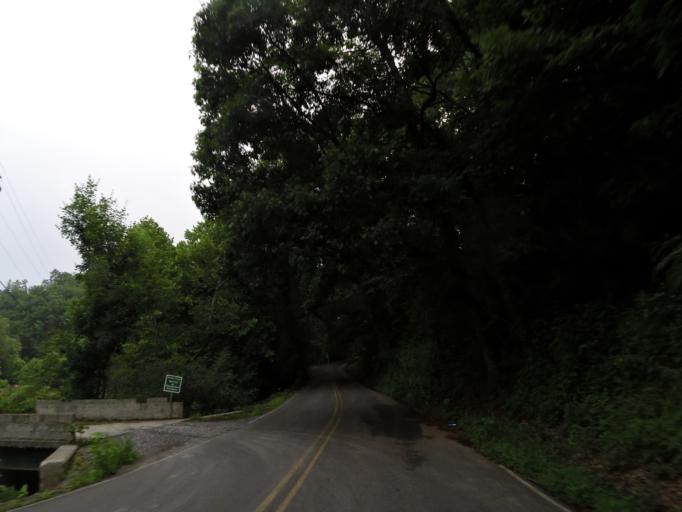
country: US
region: Tennessee
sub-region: Sevier County
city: Seymour
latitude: 35.7551
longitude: -83.6938
